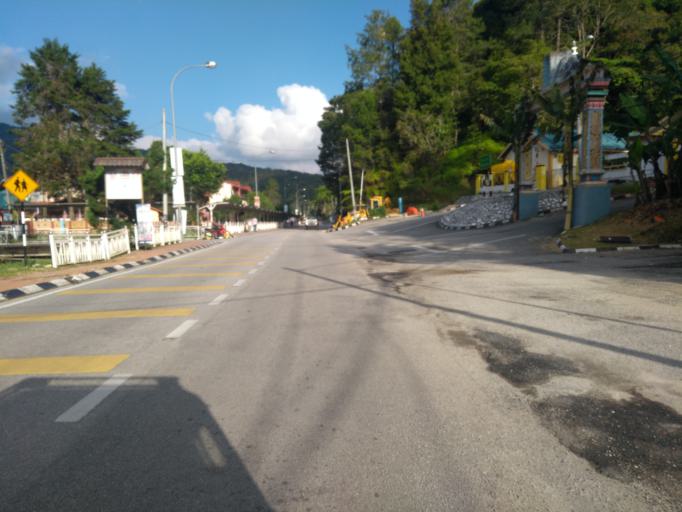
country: MY
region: Pahang
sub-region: Cameron Highlands
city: Tanah Rata
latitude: 4.4689
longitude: 101.3822
